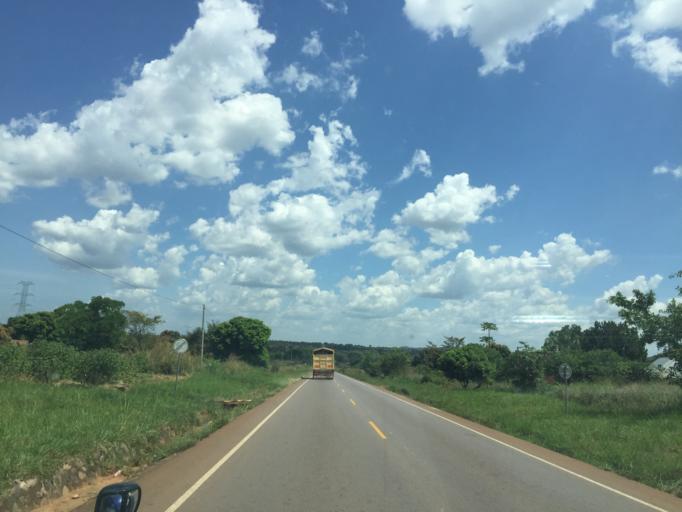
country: UG
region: Central Region
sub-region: Nakasongola District
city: Nakasongola
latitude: 1.3563
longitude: 32.3744
